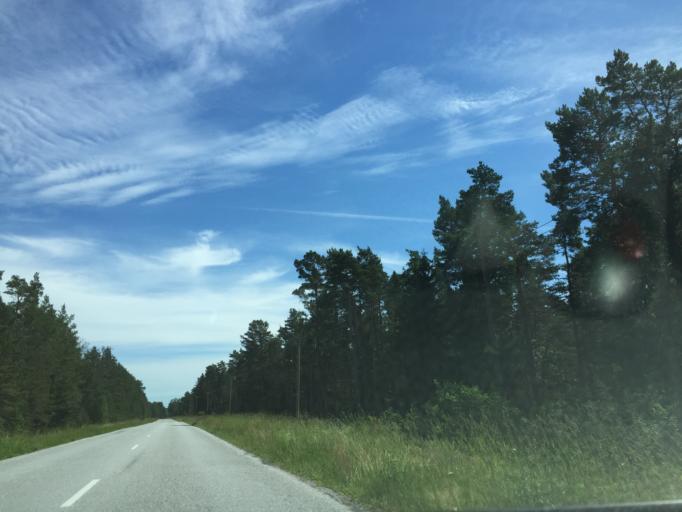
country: LV
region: Rojas
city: Roja
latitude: 57.5821
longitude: 22.6209
